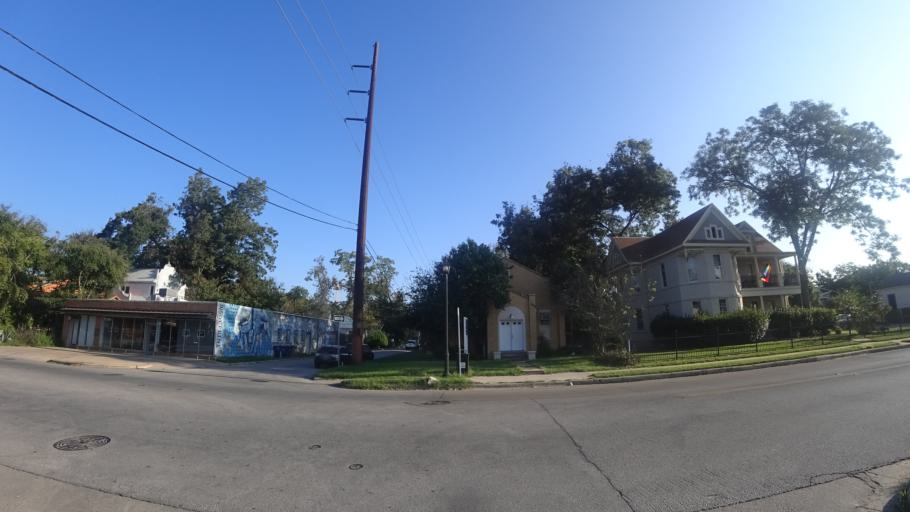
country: US
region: Texas
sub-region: Travis County
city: Austin
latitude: 30.2591
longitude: -97.7306
